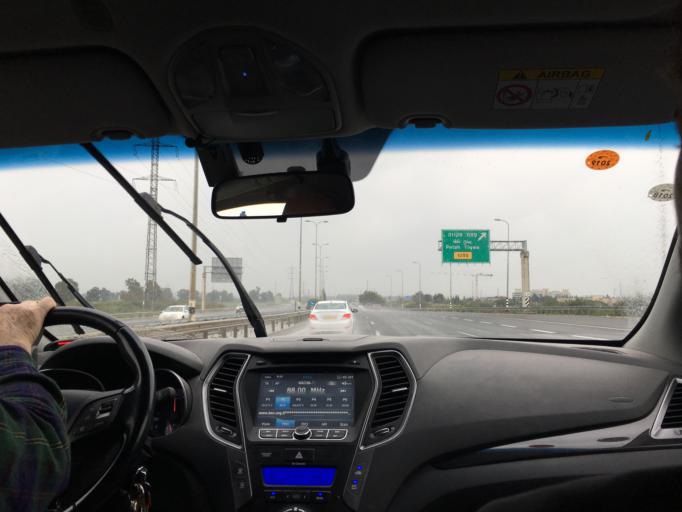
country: IL
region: Tel Aviv
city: Ramat HaSharon
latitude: 32.1215
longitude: 34.8630
